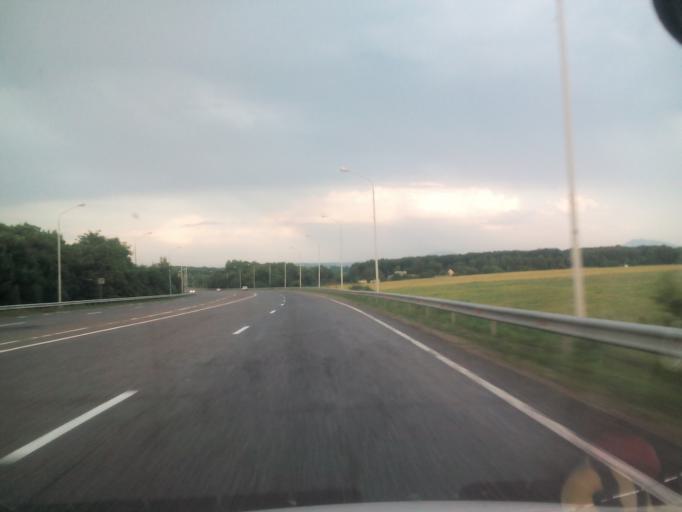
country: RU
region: Stavropol'skiy
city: Yessentuki
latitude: 44.0720
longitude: 42.8140
